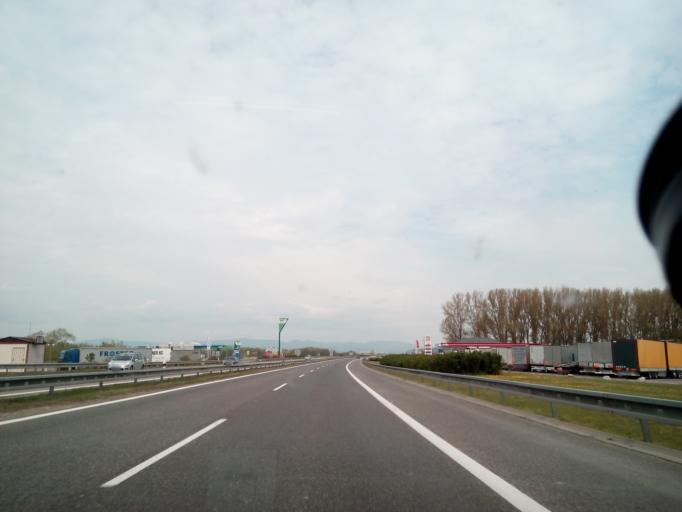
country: SK
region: Trenciansky
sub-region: Okres Nove Mesto nad Vahom
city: Nove Mesto nad Vahom
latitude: 48.7061
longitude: 17.8721
